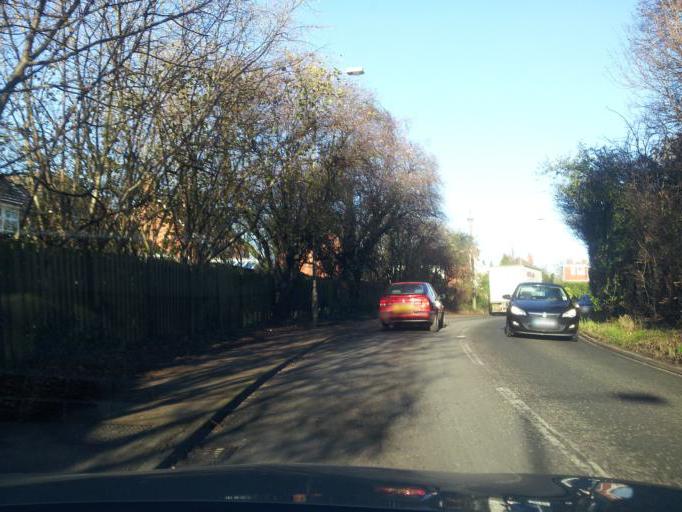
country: GB
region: England
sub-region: West Berkshire
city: Calcot
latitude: 51.4475
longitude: -1.0474
